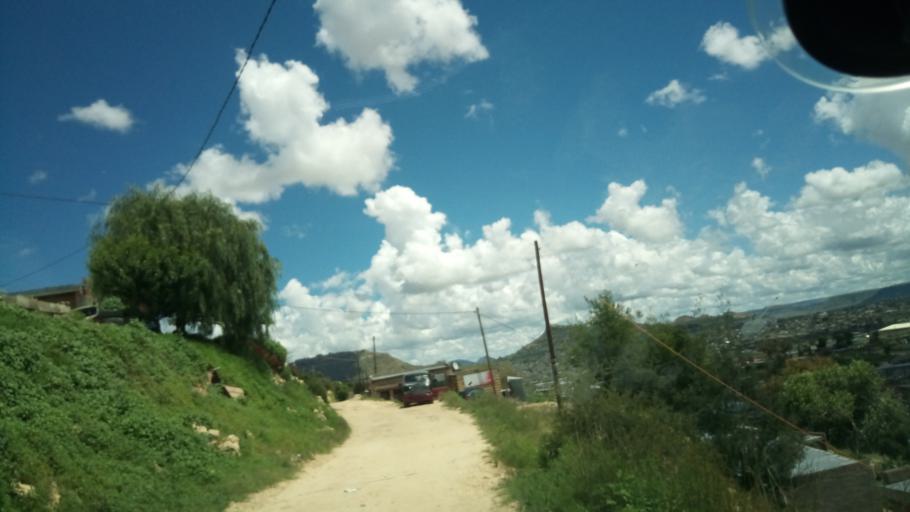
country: LS
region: Maseru
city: Maseru
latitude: -29.3514
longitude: 27.5322
